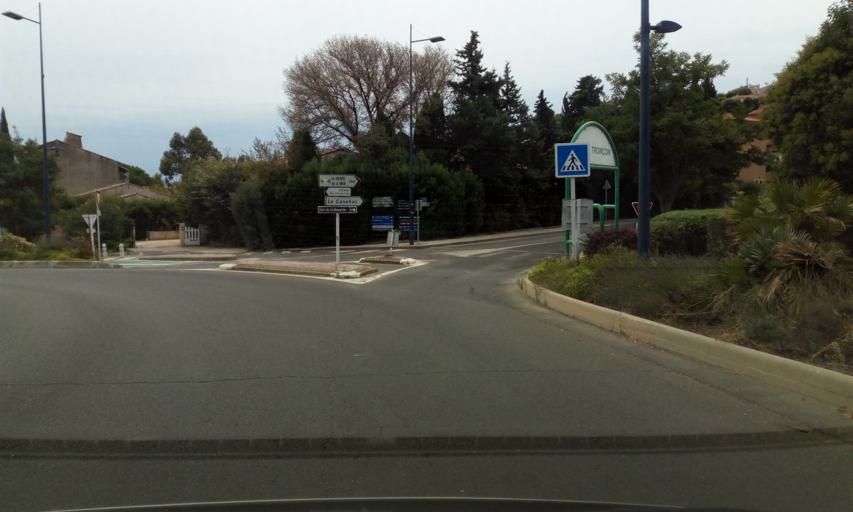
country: FR
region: Provence-Alpes-Cote d'Azur
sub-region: Departement du Var
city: Carqueiranne
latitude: 43.0959
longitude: 6.0693
